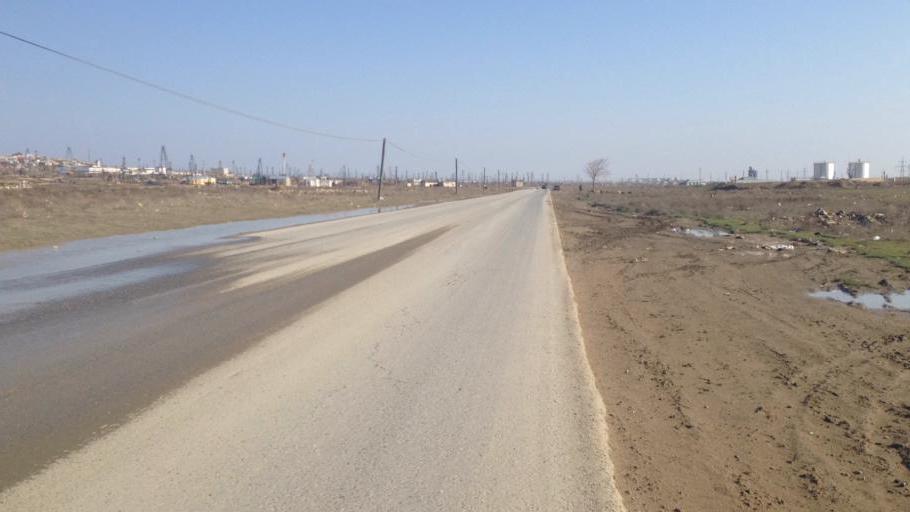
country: AZ
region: Baki
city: Balakhani
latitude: 40.4525
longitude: 49.8983
